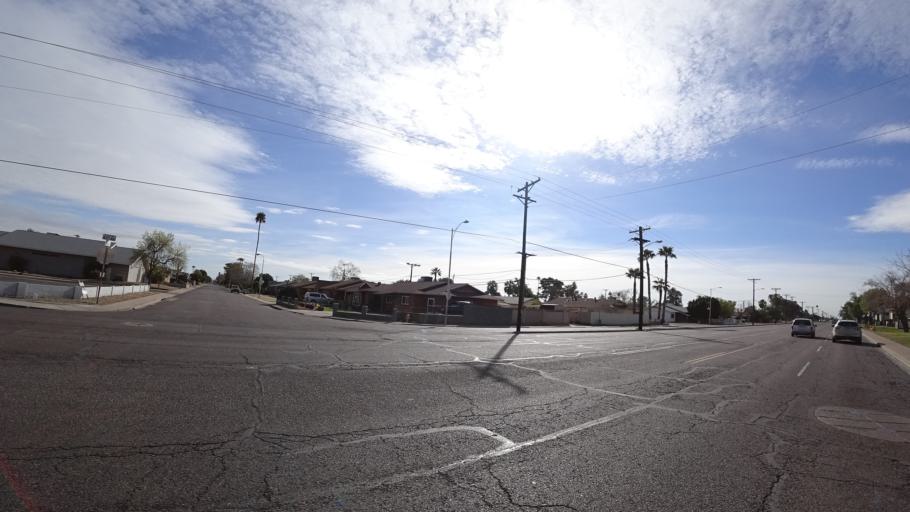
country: US
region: Arizona
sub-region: Maricopa County
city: Glendale
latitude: 33.5349
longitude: -112.1516
